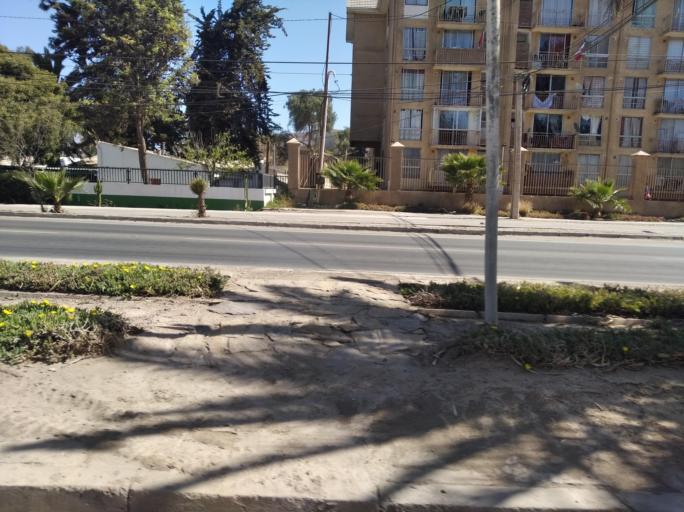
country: CL
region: Atacama
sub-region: Provincia de Copiapo
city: Copiapo
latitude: -27.3903
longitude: -70.3115
